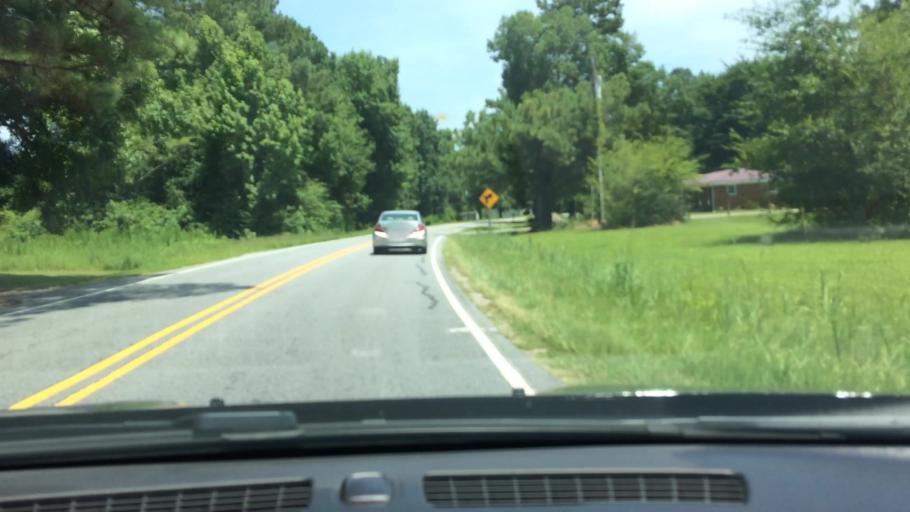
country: US
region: North Carolina
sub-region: Beaufort County
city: Washington
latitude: 35.5687
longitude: -77.1862
